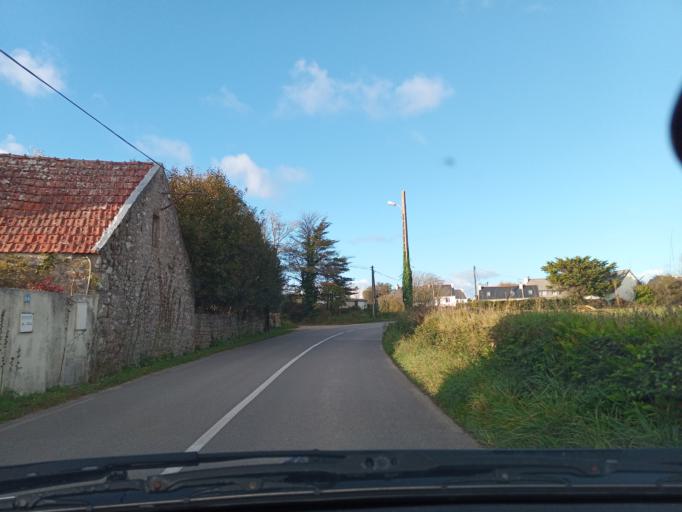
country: FR
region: Brittany
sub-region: Departement du Finistere
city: Esquibien
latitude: 48.0182
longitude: -4.5648
